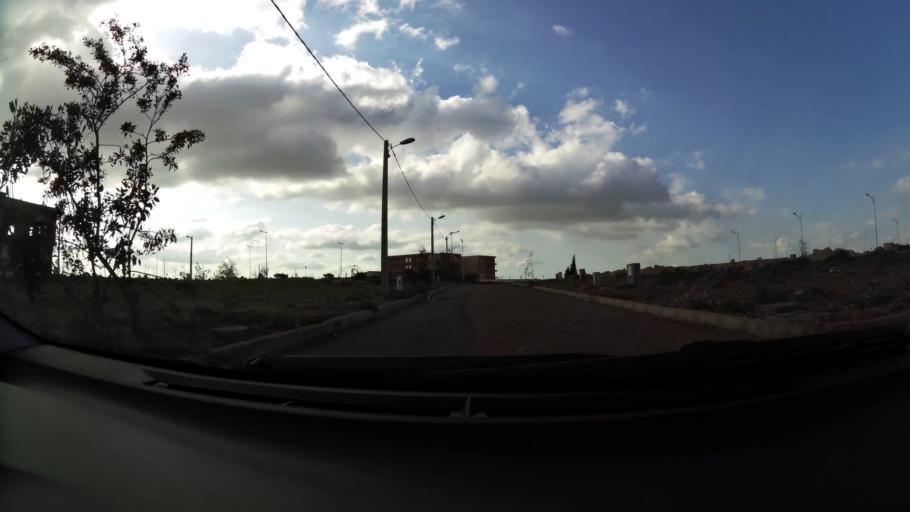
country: MA
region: Chaouia-Ouardigha
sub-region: Settat Province
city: Settat
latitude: 33.0103
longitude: -7.6399
